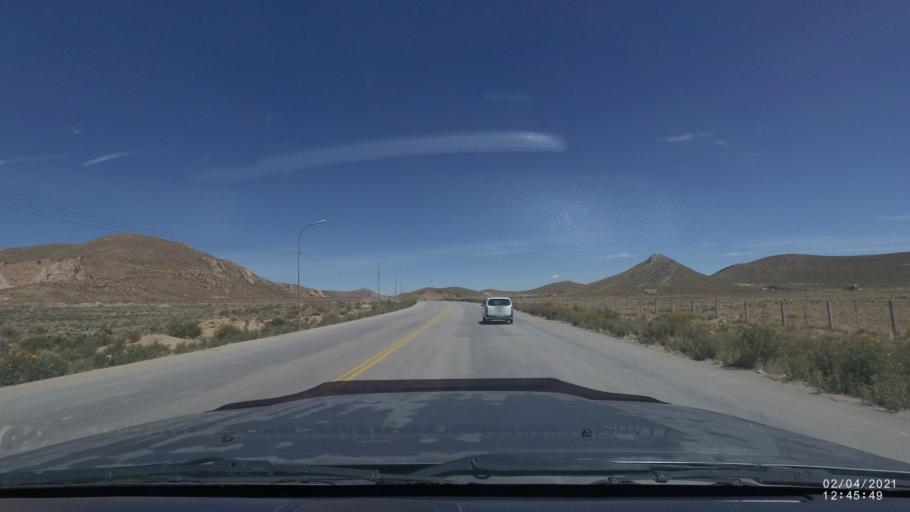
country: BO
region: Oruro
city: Oruro
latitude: -17.9388
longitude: -67.1367
